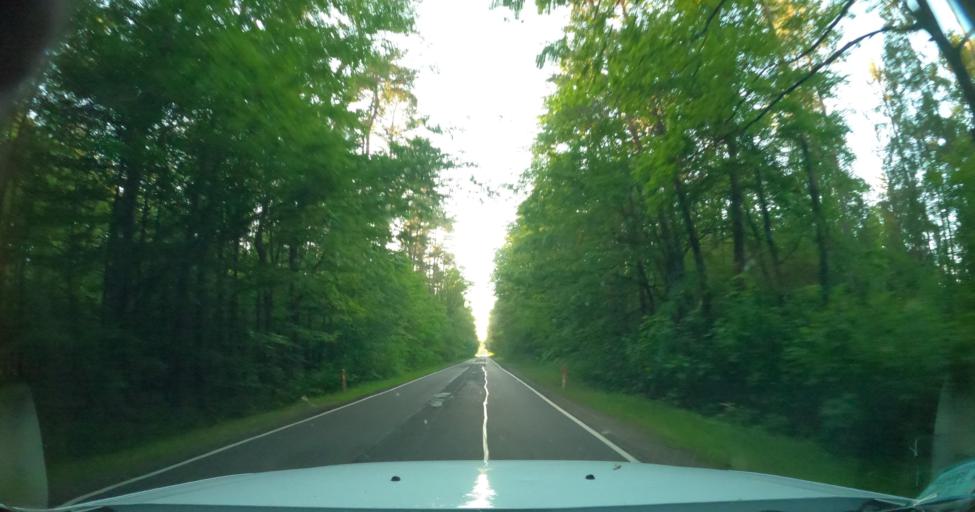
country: PL
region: Pomeranian Voivodeship
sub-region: Powiat bytowski
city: Czarna Dabrowka
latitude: 54.3819
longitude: 17.4868
